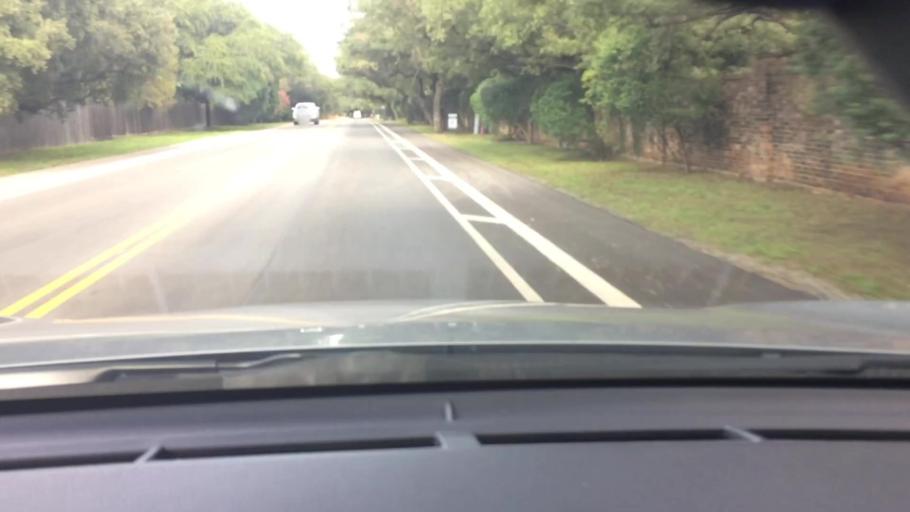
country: US
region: Texas
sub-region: Bexar County
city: Shavano Park
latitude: 29.5587
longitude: -98.5460
